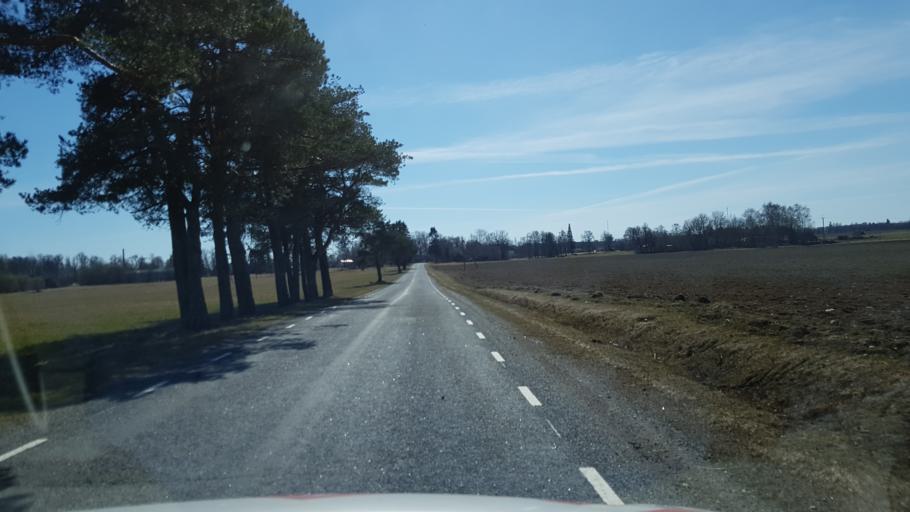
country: EE
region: Laeaene-Virumaa
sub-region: Vinni vald
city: Vinni
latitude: 59.1038
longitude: 26.5258
